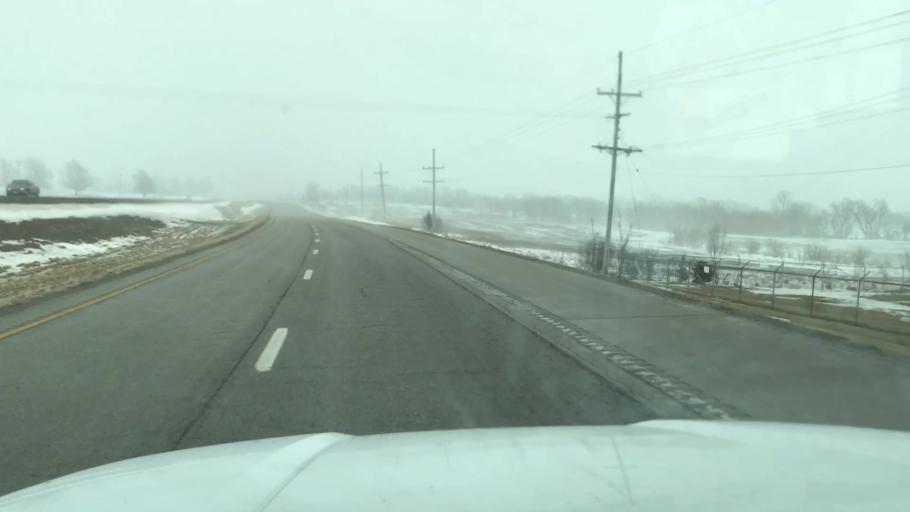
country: US
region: Missouri
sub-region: Clinton County
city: Cameron
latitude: 39.7544
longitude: -94.3359
